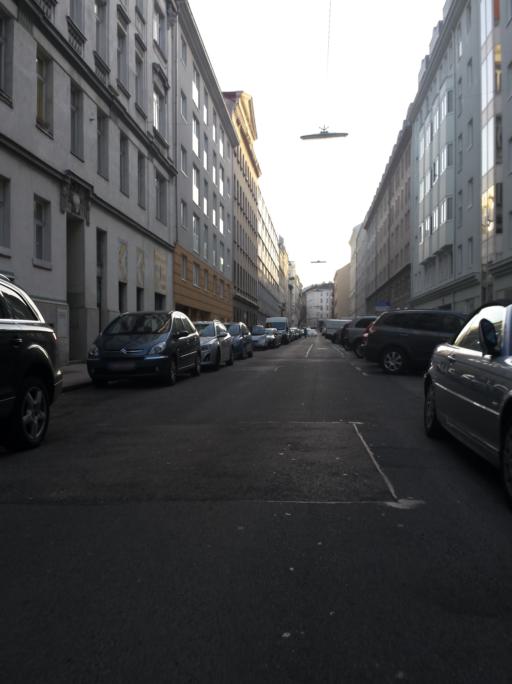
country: AT
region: Vienna
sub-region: Wien Stadt
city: Vienna
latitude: 48.1949
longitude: 16.3961
